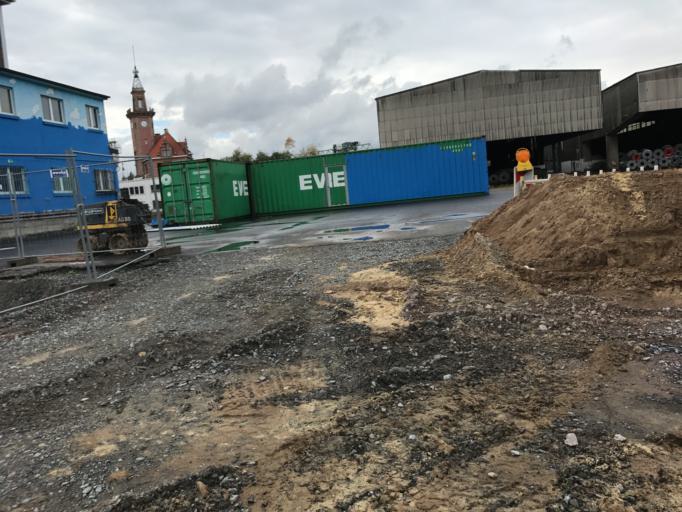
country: DE
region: North Rhine-Westphalia
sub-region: Regierungsbezirk Arnsberg
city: Dortmund
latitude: 51.5254
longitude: 7.4452
